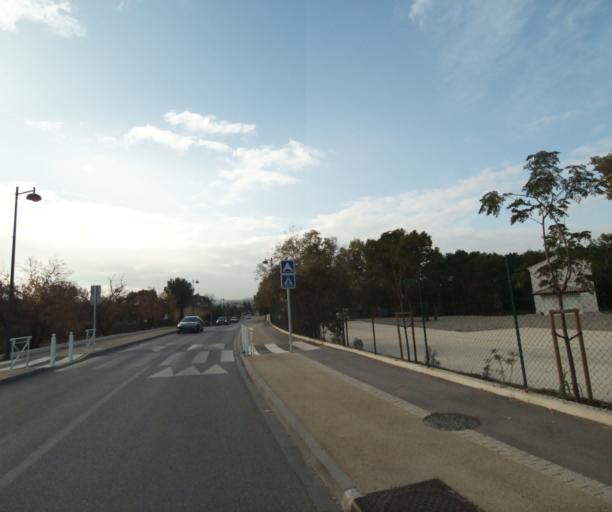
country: FR
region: Provence-Alpes-Cote d'Azur
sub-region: Departement des Bouches-du-Rhone
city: Saint-Victoret
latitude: 43.4211
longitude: 5.2444
